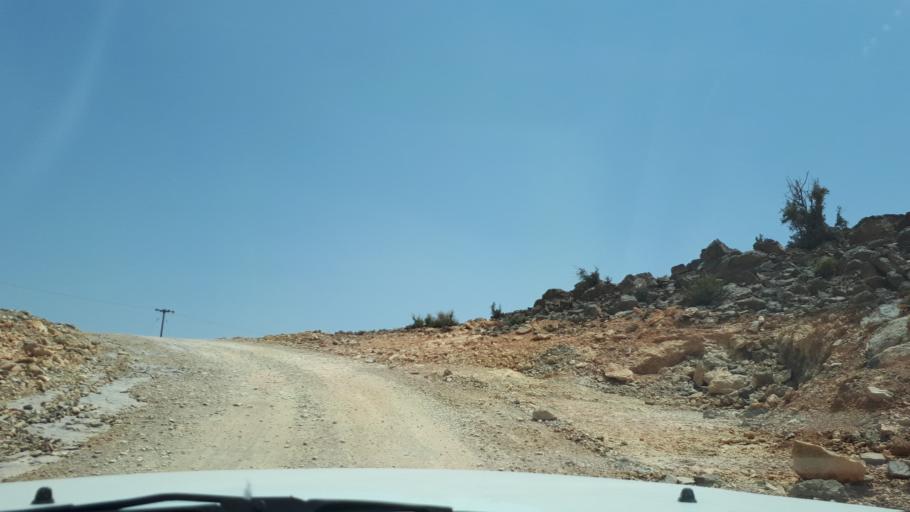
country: OM
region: Muhafazat ad Dakhiliyah
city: Bahla'
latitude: 23.2030
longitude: 57.2007
